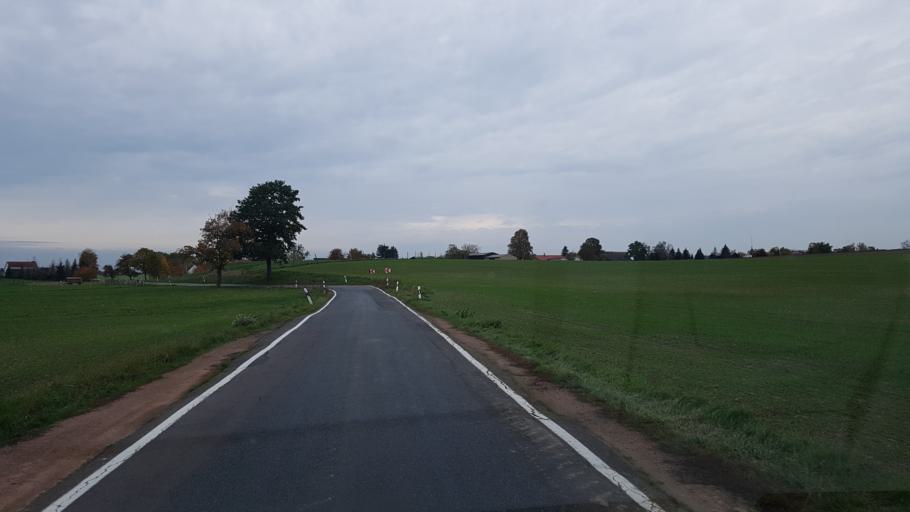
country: DE
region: Saxony
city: Dahlen
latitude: 51.3795
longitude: 12.9531
